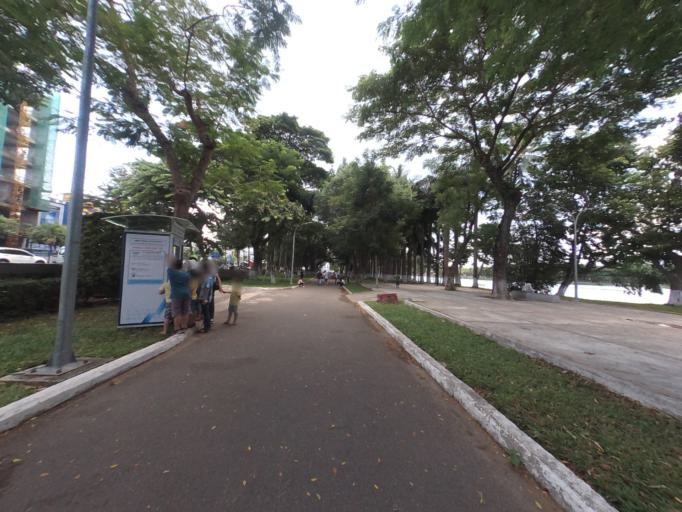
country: VN
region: Da Nang
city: Da Nang
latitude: 16.0611
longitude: 108.2052
